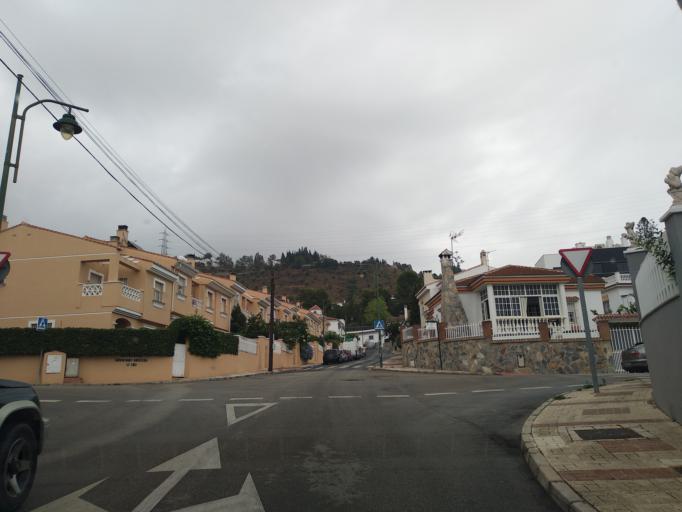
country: ES
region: Andalusia
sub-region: Provincia de Malaga
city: Malaga
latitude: 36.7404
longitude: -4.4780
